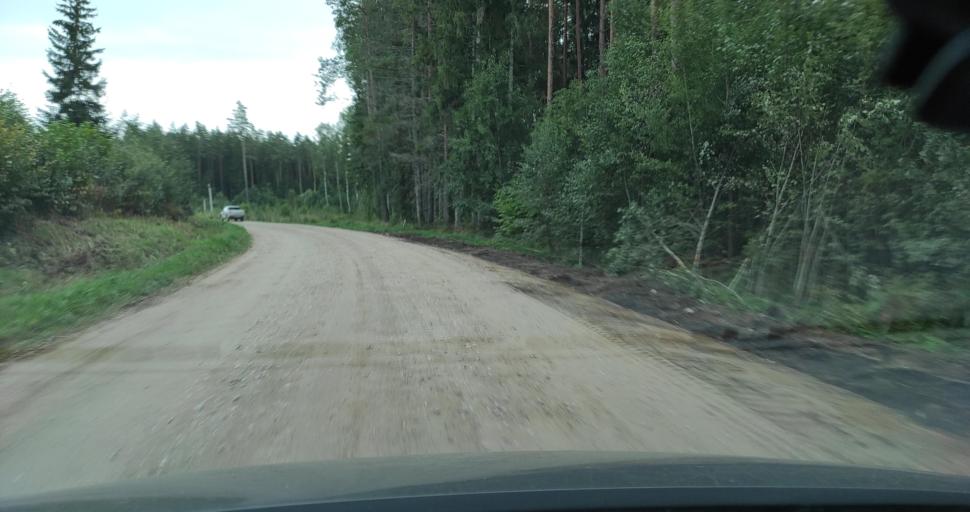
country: LV
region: Talsu Rajons
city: Stende
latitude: 57.0435
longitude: 22.3068
